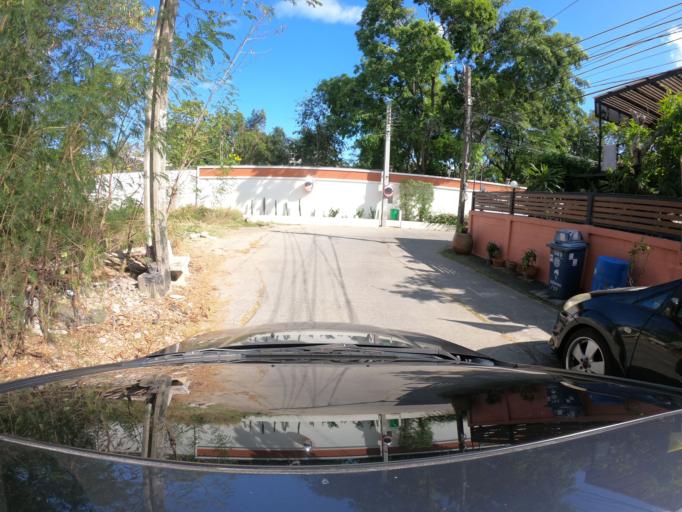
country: TH
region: Bangkok
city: Bang Na
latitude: 13.6517
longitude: 100.6274
